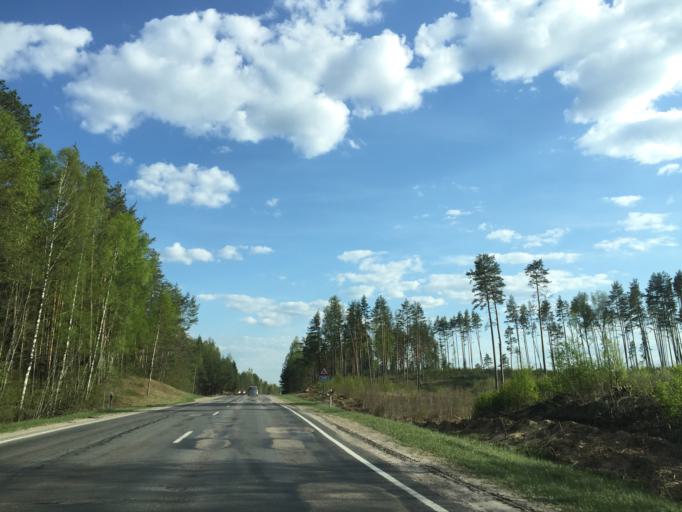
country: LV
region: Pargaujas
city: Stalbe
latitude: 57.3134
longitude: 24.9238
